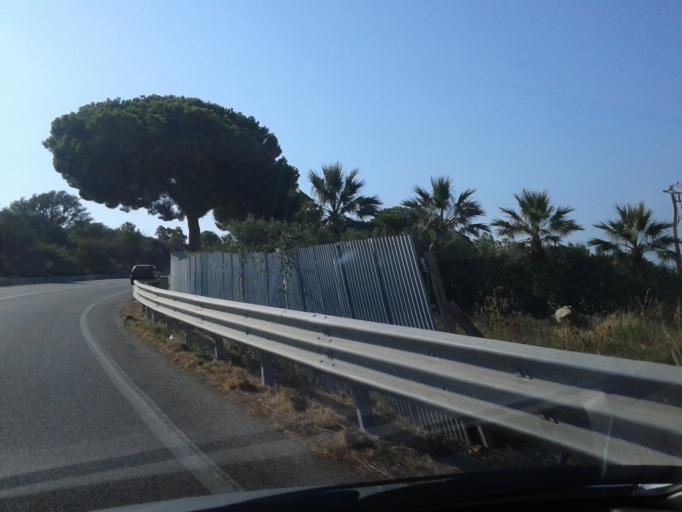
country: IT
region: Sicily
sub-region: Palermo
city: Finale
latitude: 38.0235
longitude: 14.1507
